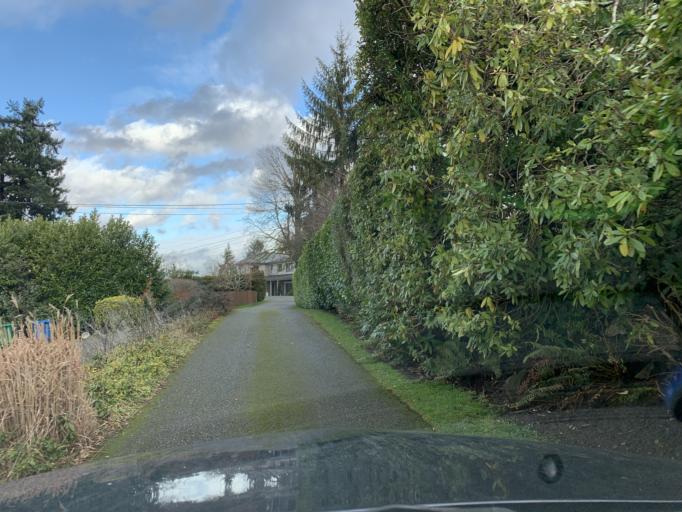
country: US
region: Washington
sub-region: King County
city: Mercer Island
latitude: 47.5859
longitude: -122.2452
